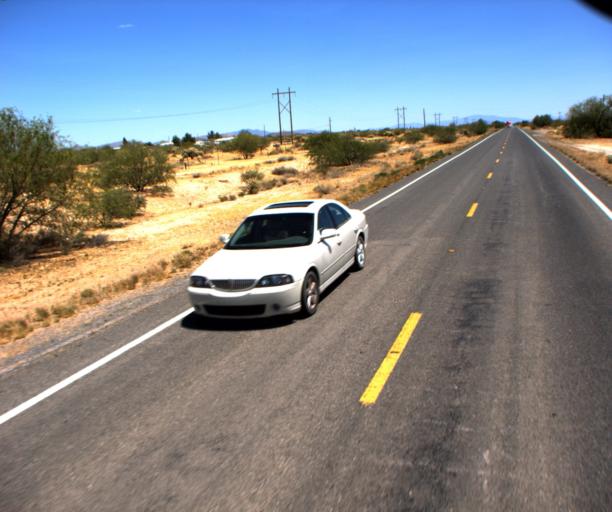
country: US
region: Arizona
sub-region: Pinal County
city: Florence
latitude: 32.9239
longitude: -111.3007
